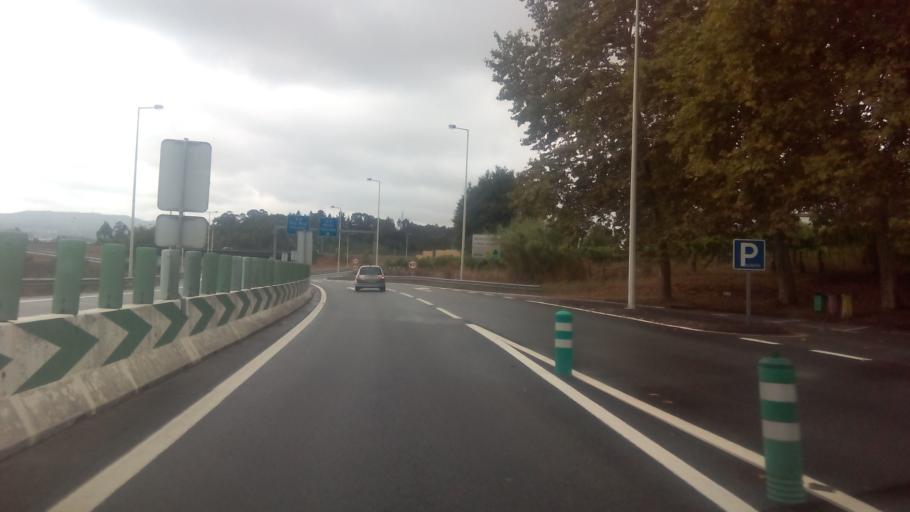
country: PT
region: Porto
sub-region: Paredes
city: Casteloes de Cepeda
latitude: 41.2014
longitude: -8.3379
